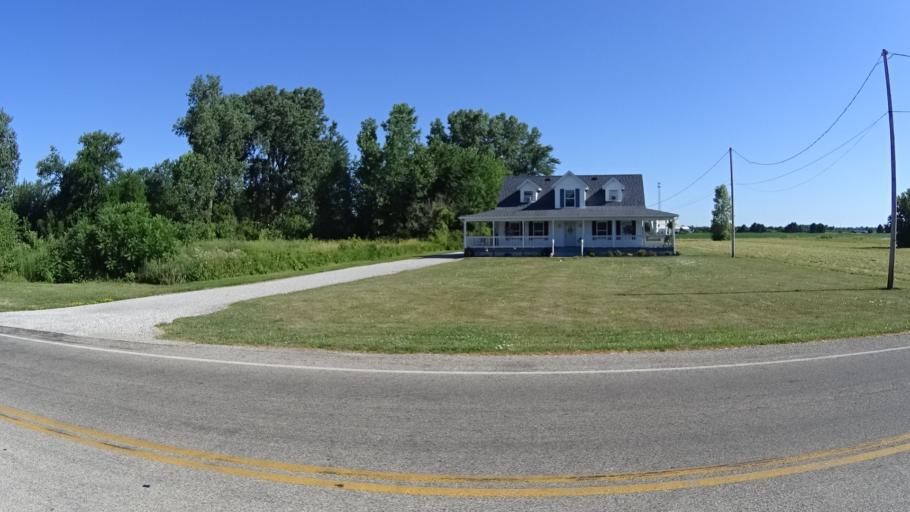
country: US
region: Ohio
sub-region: Erie County
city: Sandusky
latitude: 41.3970
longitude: -82.7305
